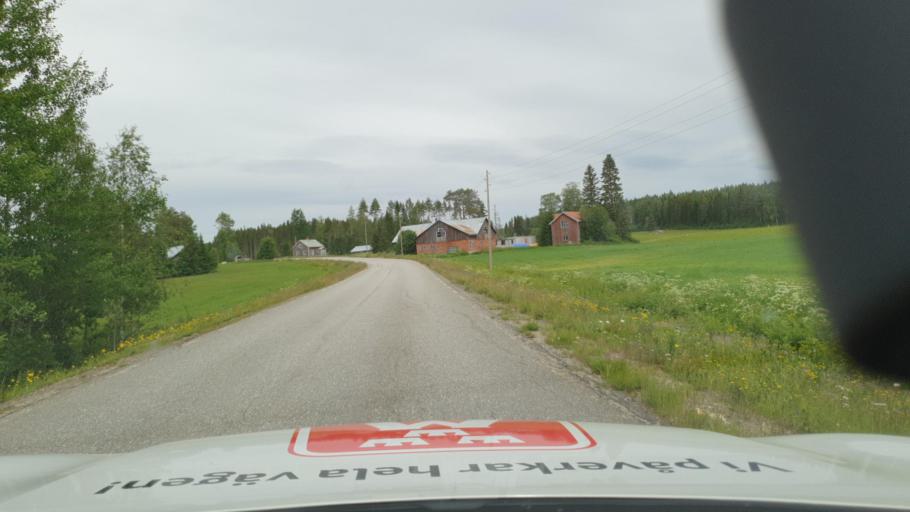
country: SE
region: Vaesterbotten
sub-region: Robertsfors Kommun
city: Robertsfors
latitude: 64.2847
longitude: 20.6547
